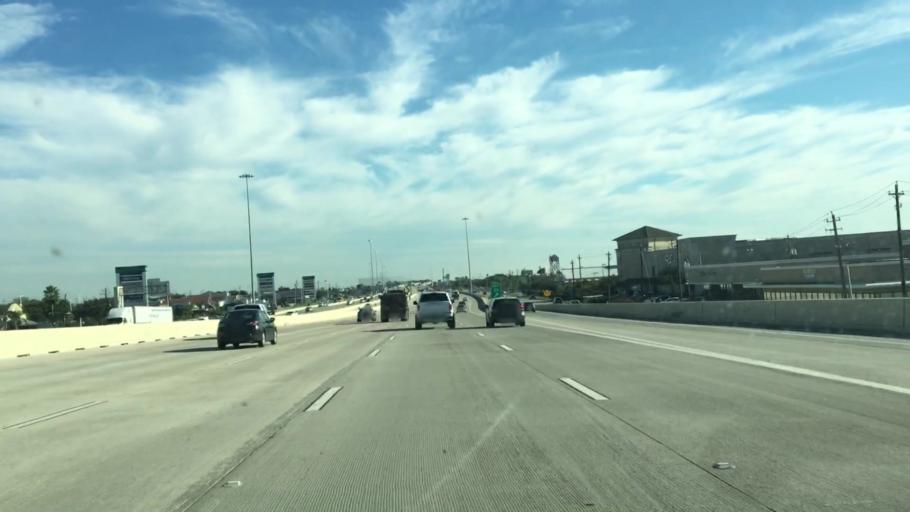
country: US
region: Texas
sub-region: Harris County
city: Webster
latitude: 29.5392
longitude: -95.1407
